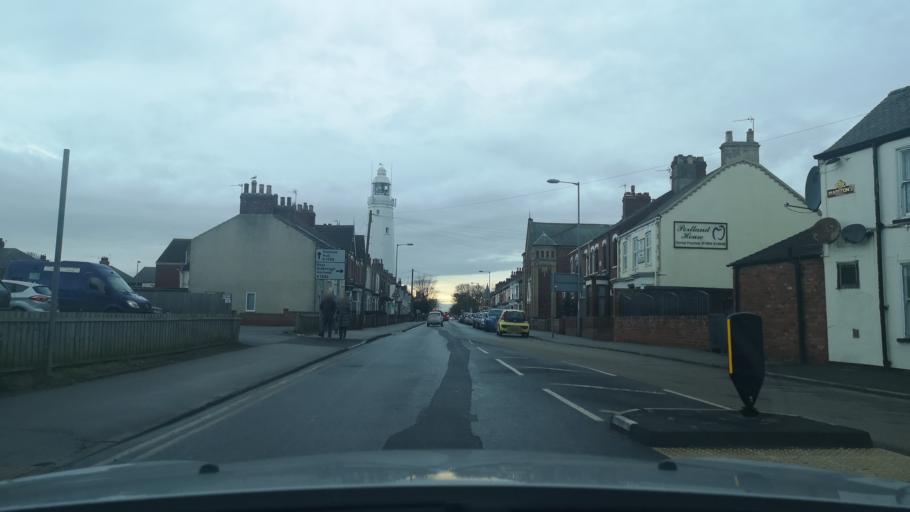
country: GB
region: England
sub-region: East Riding of Yorkshire
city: Withernsea
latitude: 53.7313
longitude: 0.0313
